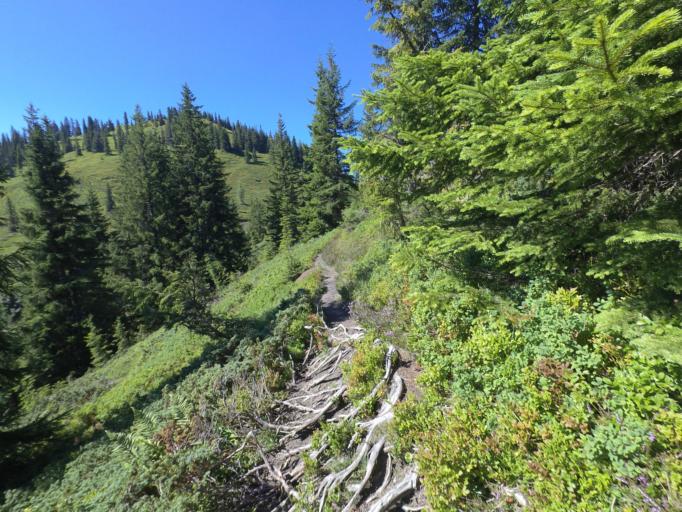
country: AT
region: Salzburg
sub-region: Politischer Bezirk Sankt Johann im Pongau
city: Goldegg
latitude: 47.3563
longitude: 13.0750
